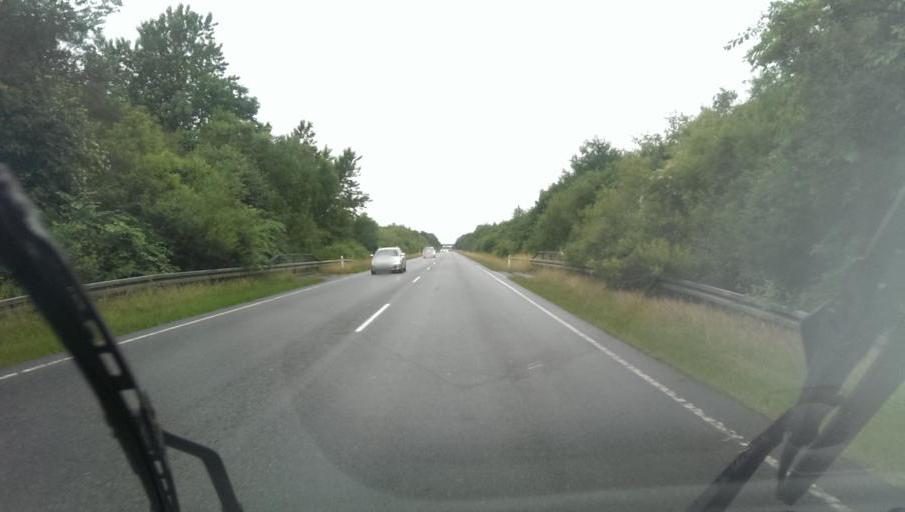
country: DK
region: South Denmark
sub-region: Esbjerg Kommune
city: Esbjerg
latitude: 55.5259
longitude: 8.4427
